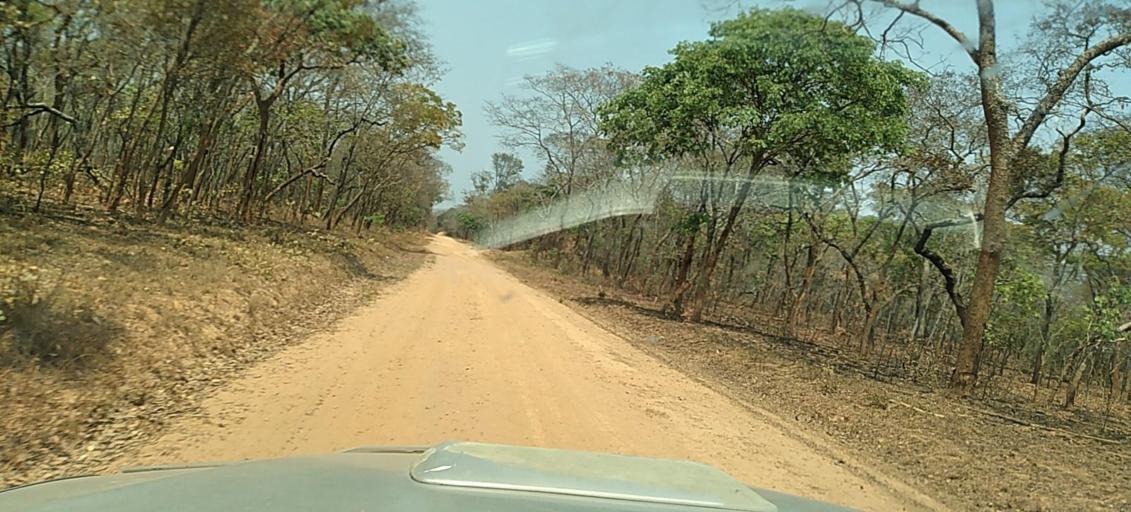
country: ZM
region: North-Western
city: Kasempa
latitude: -13.6620
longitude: 26.2733
